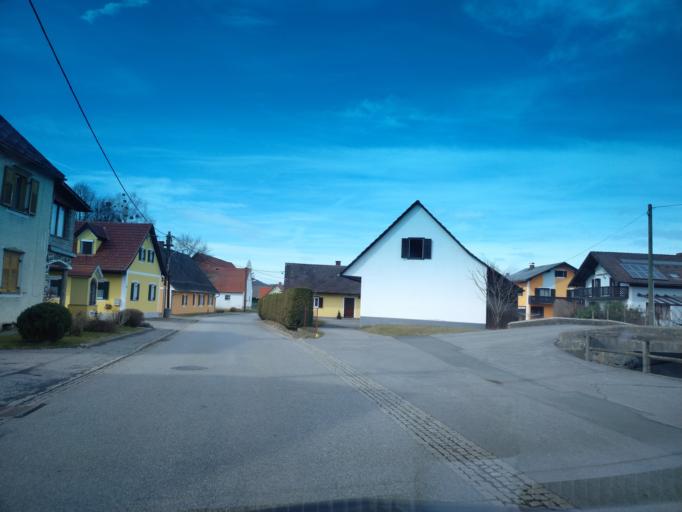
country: AT
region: Styria
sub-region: Politischer Bezirk Leibnitz
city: Grossklein
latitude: 46.7384
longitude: 15.4413
